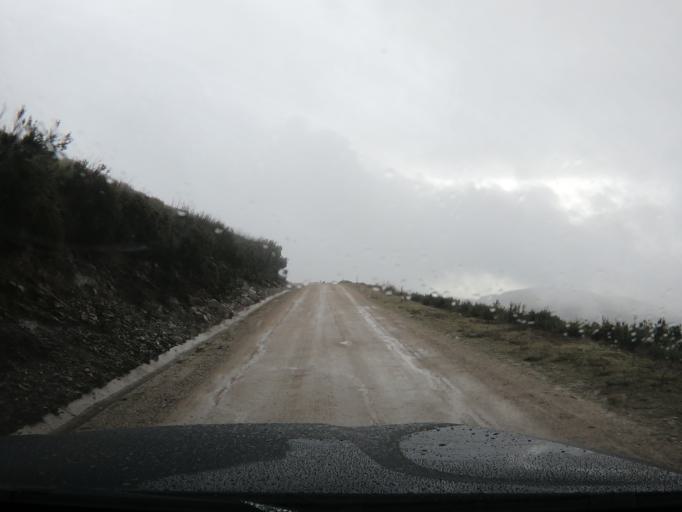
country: PT
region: Vila Real
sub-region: Vila Real
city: Vila Real
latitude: 41.3273
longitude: -7.8445
